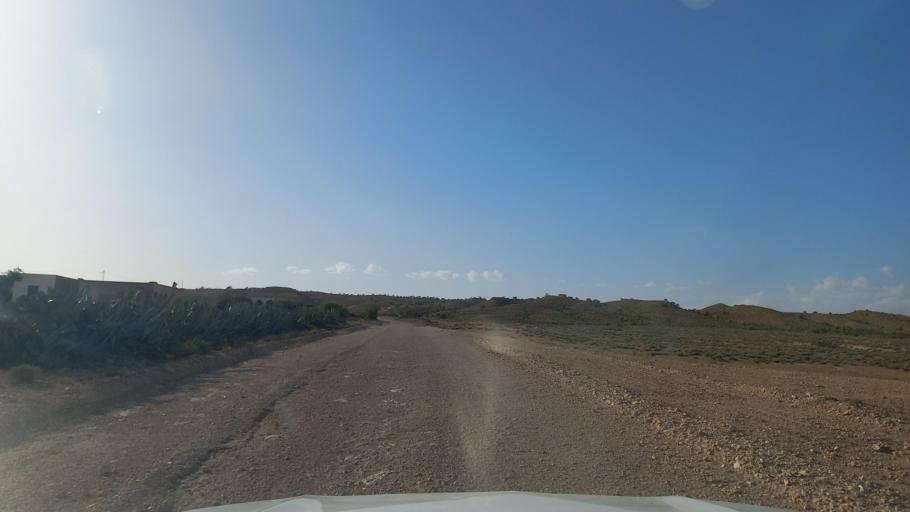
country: TN
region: Al Qasrayn
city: Sbiba
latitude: 35.3640
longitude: 8.9998
